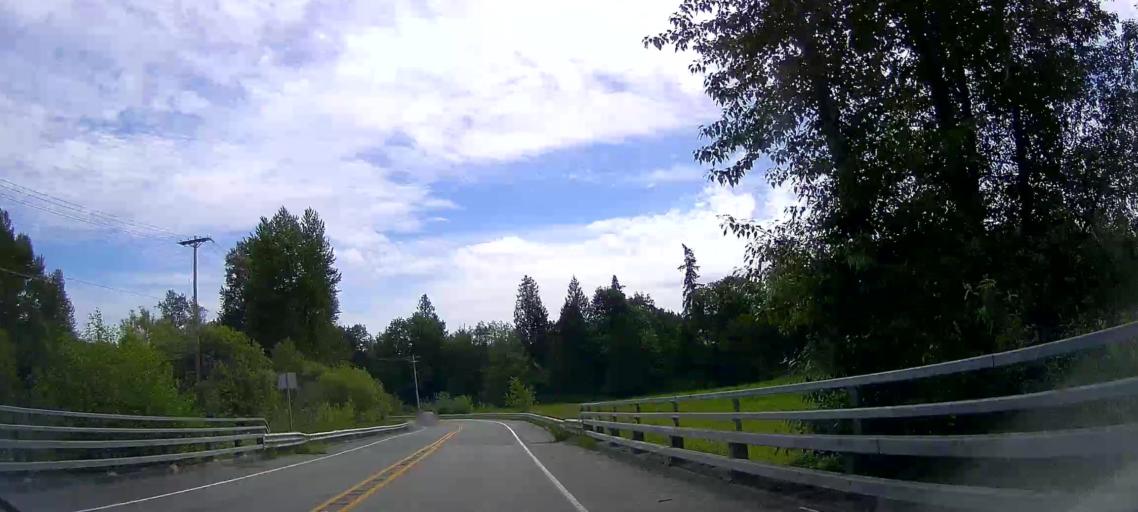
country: US
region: Washington
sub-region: Snohomish County
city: Bryant
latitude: 48.2386
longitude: -122.2047
